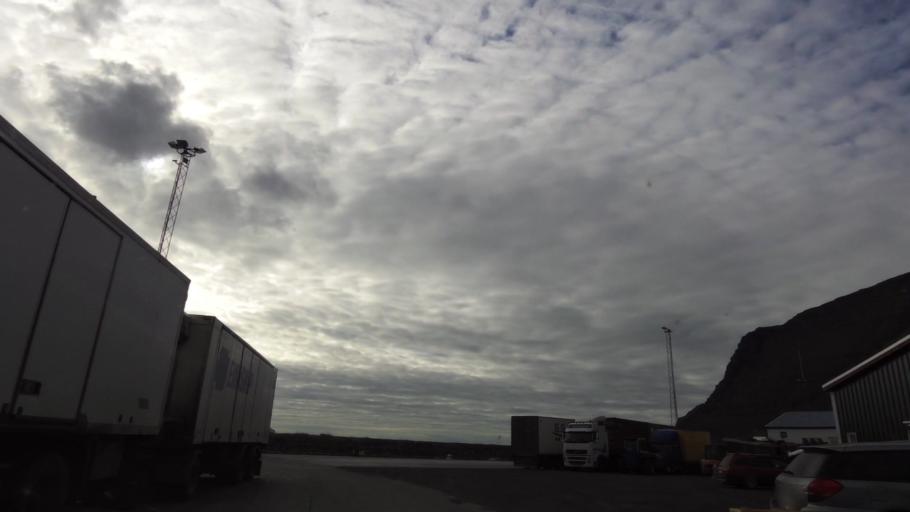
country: IS
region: West
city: Olafsvik
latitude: 65.5960
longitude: -24.0048
